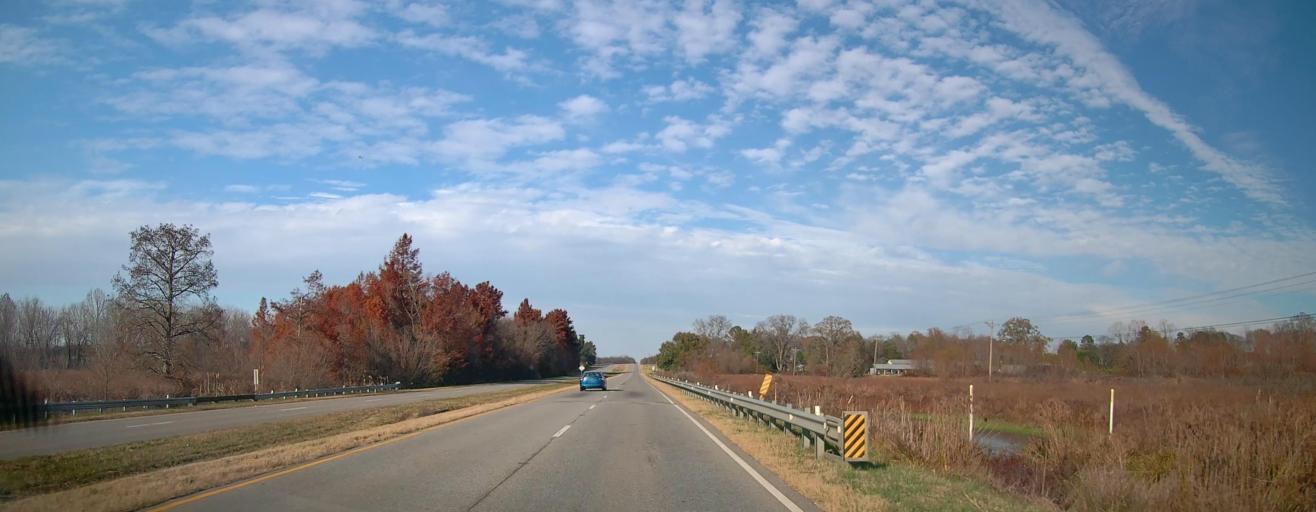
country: US
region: Alabama
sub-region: Morgan County
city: Decatur
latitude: 34.6753
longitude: -86.9497
